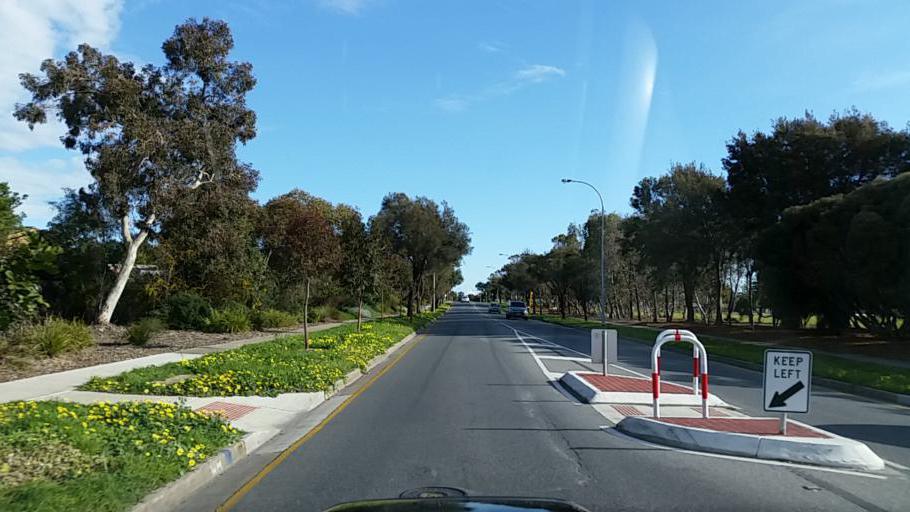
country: AU
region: South Australia
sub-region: Charles Sturt
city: West Lakes Shore
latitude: -34.8628
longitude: 138.4868
